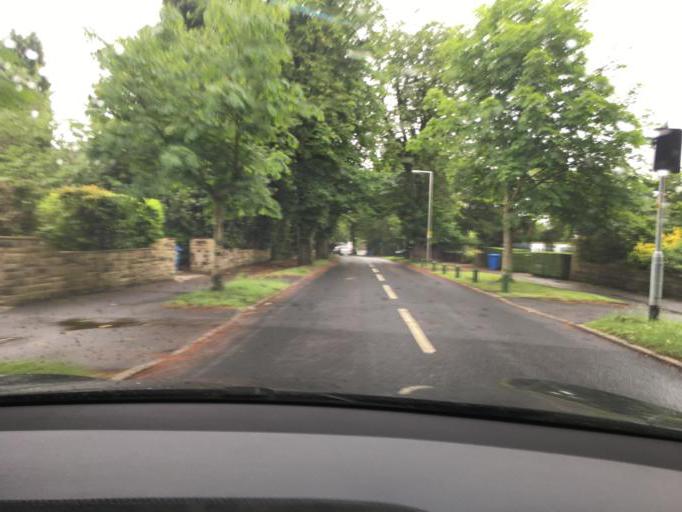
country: GB
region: England
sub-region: Borough of Stockport
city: Bramhall
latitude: 53.3772
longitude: -2.1654
